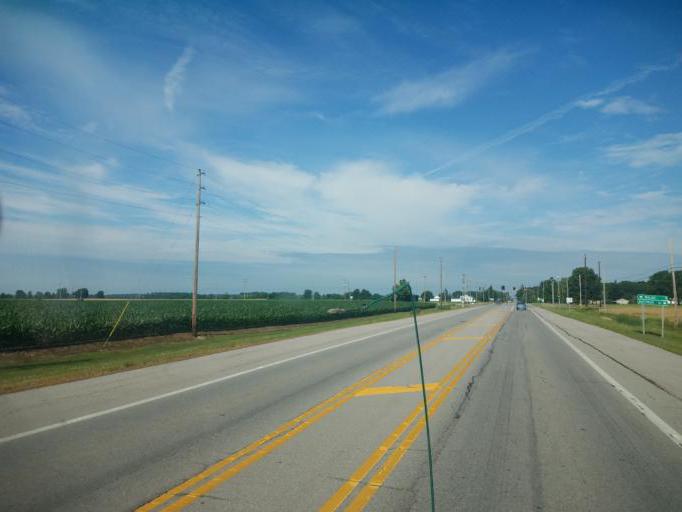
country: US
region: Ohio
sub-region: Marion County
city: Marion
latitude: 40.5835
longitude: -83.0383
